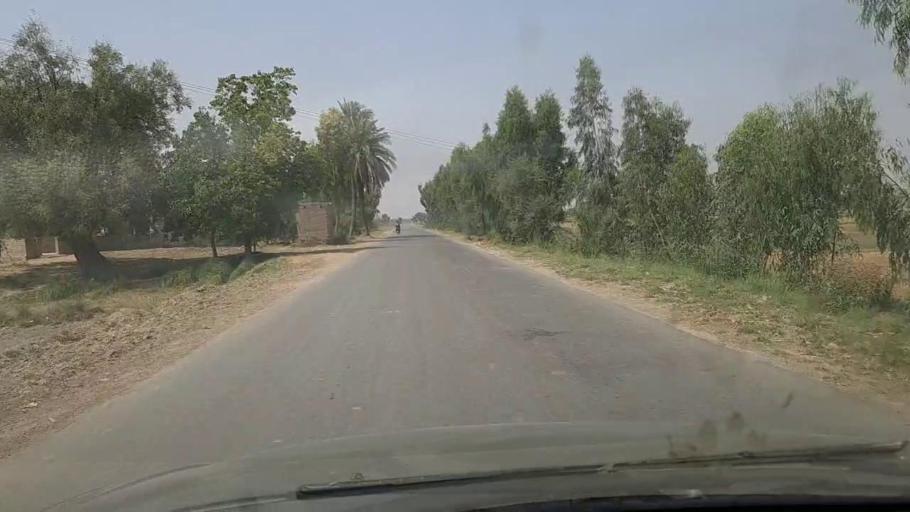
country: PK
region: Sindh
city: Khanpur
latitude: 27.8663
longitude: 69.4442
